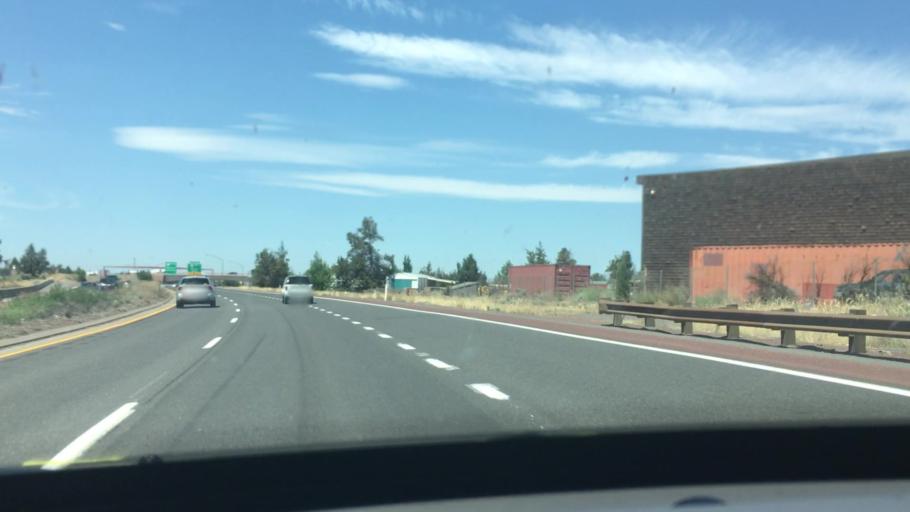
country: US
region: Oregon
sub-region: Deschutes County
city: Bend
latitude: 44.0939
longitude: -121.3004
